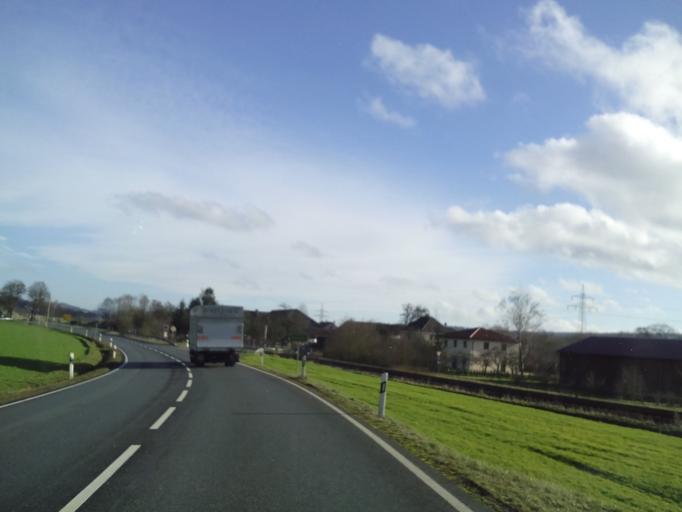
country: DE
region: Bavaria
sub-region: Upper Franconia
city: Altenkunstadt
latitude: 50.1260
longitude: 11.2923
